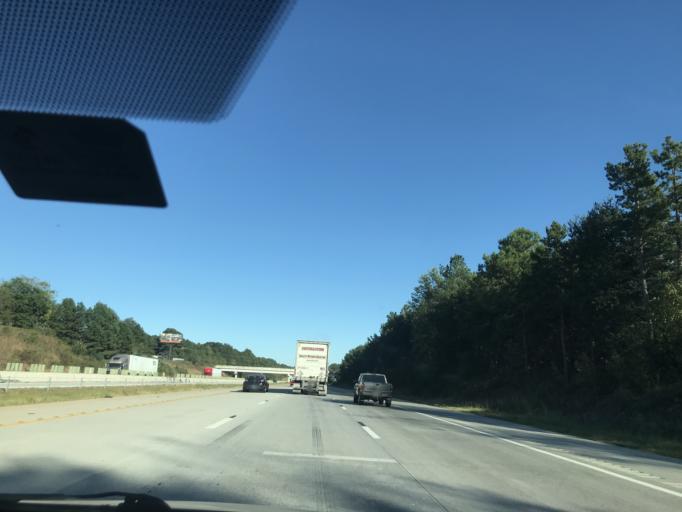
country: US
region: South Carolina
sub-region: Spartanburg County
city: Valley Falls
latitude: 35.0118
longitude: -81.9320
